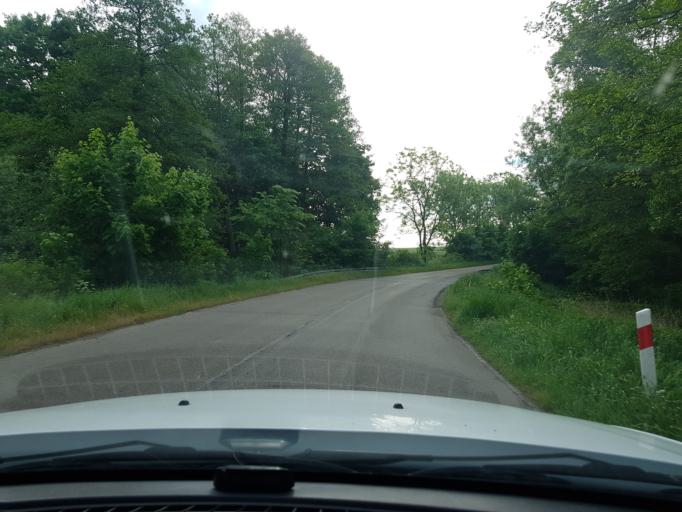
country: PL
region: West Pomeranian Voivodeship
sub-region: Powiat stargardzki
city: Chociwel
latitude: 53.4683
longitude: 15.3588
